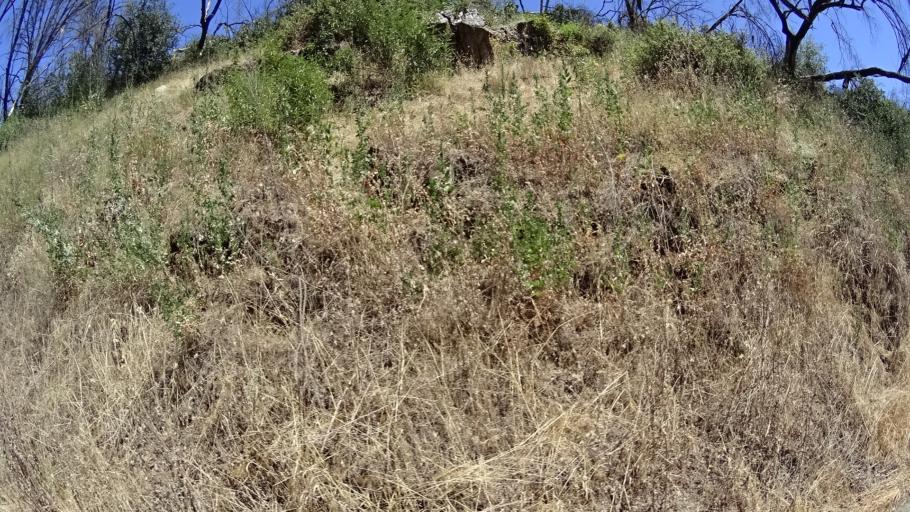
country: US
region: California
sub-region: Calaveras County
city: San Andreas
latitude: 38.2850
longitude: -120.6704
